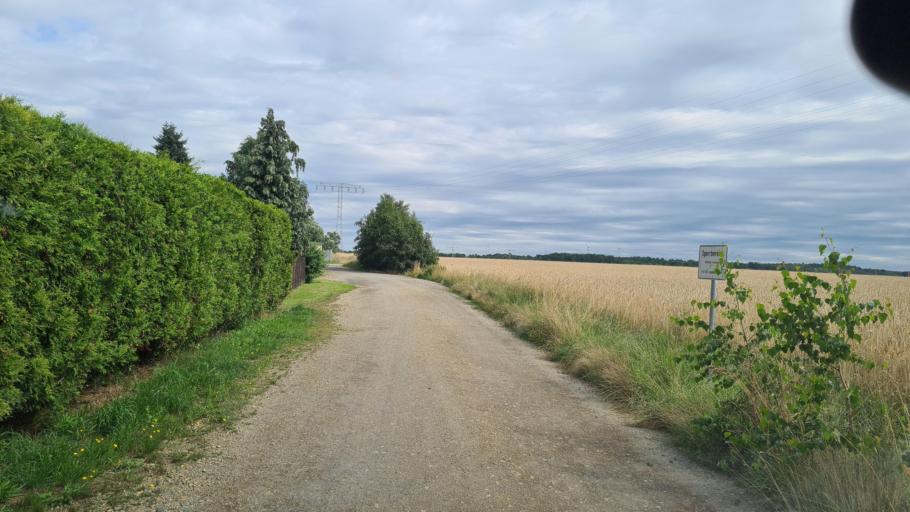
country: DE
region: Brandenburg
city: Grossraschen
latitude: 51.5523
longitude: 14.0633
